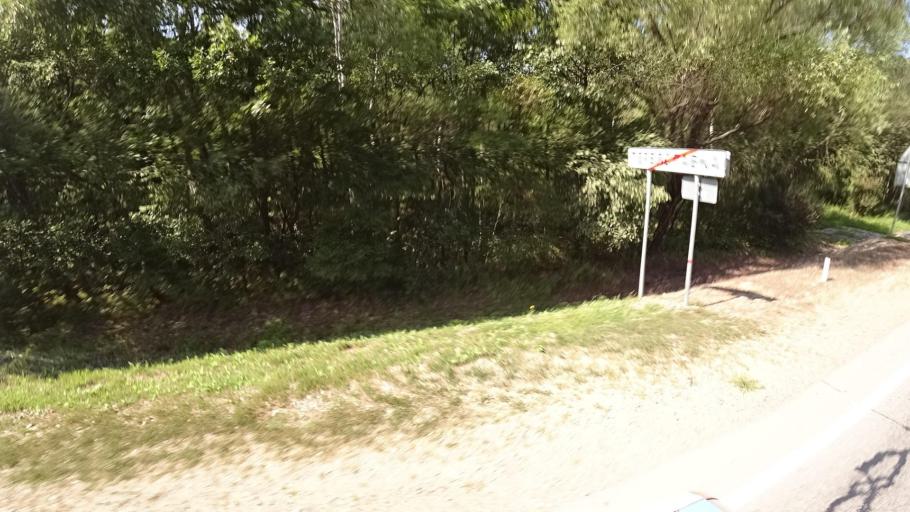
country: RU
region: Khabarovsk Krai
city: Khor
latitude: 47.9764
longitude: 135.0838
